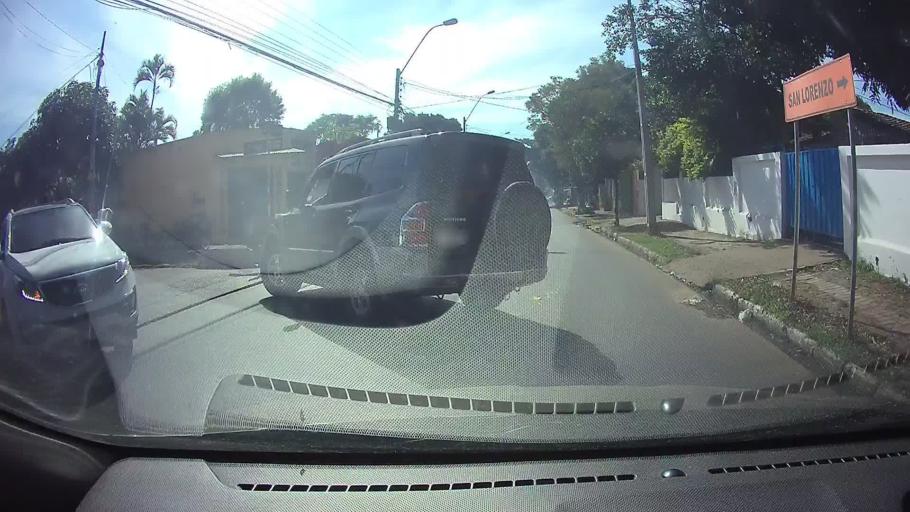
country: PY
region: Central
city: Fernando de la Mora
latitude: -25.3311
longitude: -57.5577
